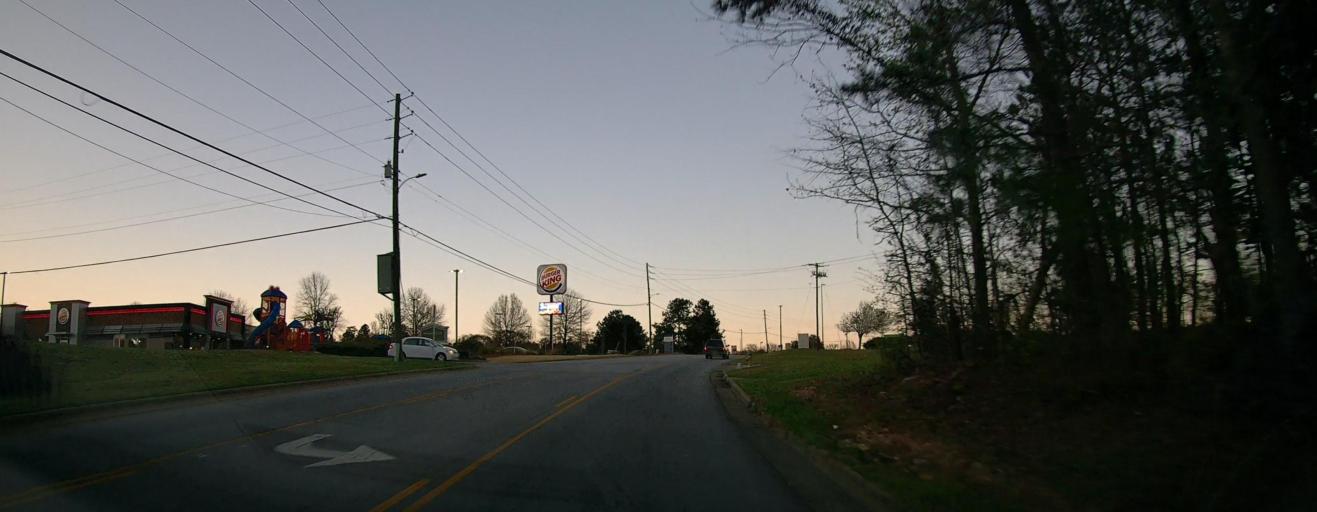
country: US
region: Alabama
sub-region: Russell County
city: Phenix City
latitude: 32.4951
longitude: -85.0184
